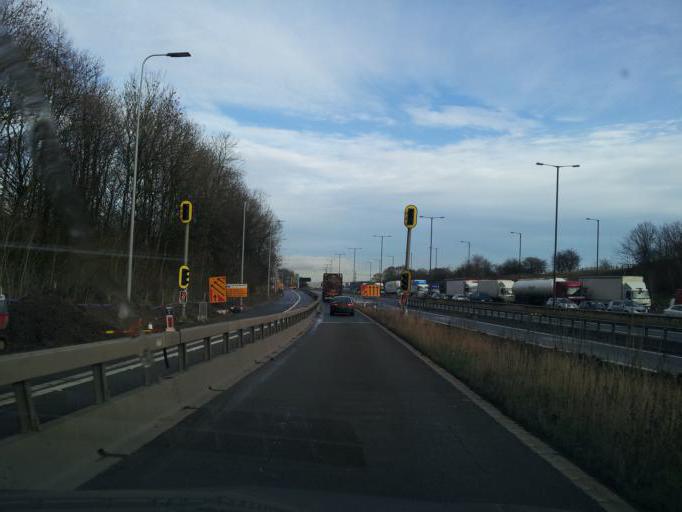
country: GB
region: England
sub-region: Manchester
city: Heywood
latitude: 53.5780
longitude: -2.2041
